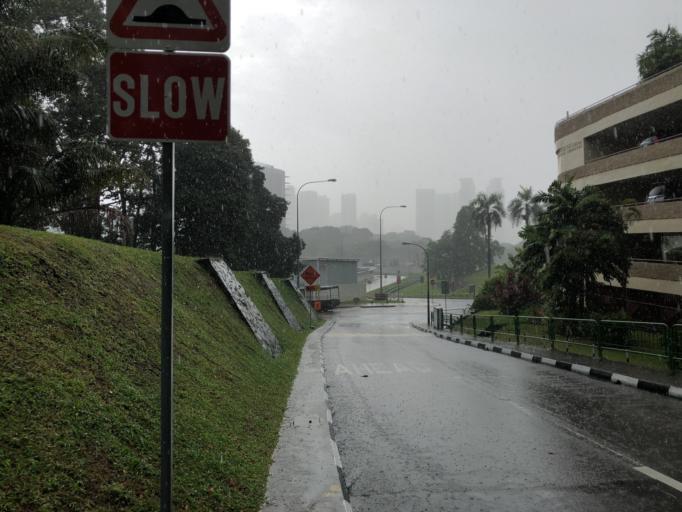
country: SG
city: Singapore
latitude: 1.2826
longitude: 103.8397
